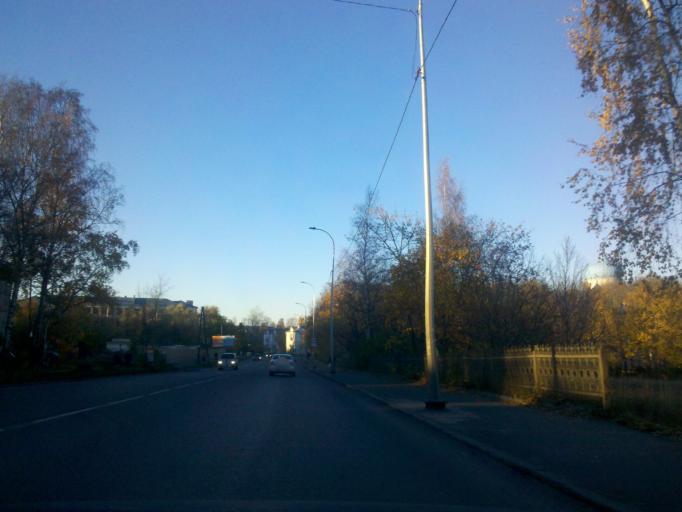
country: RU
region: Republic of Karelia
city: Petrozavodsk
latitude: 61.7785
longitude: 34.3897
